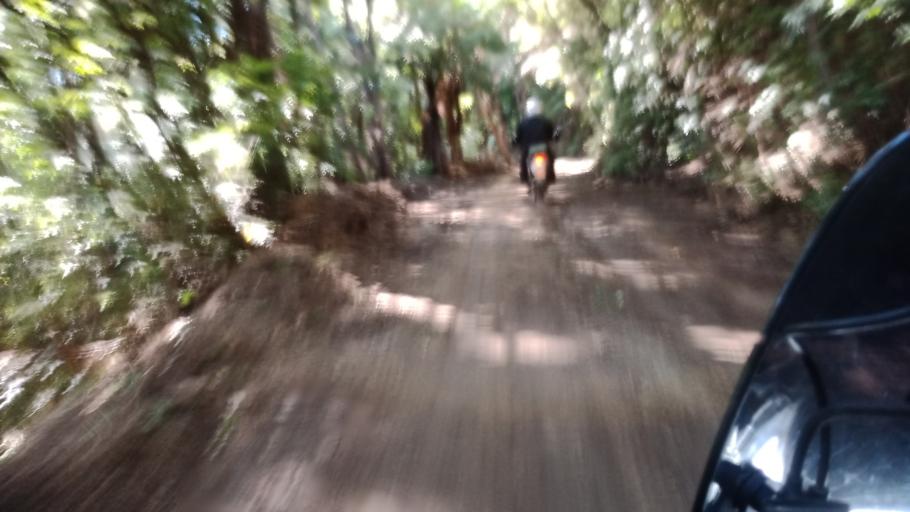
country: NZ
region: Hawke's Bay
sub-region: Wairoa District
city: Wairoa
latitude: -38.9995
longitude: 177.0649
